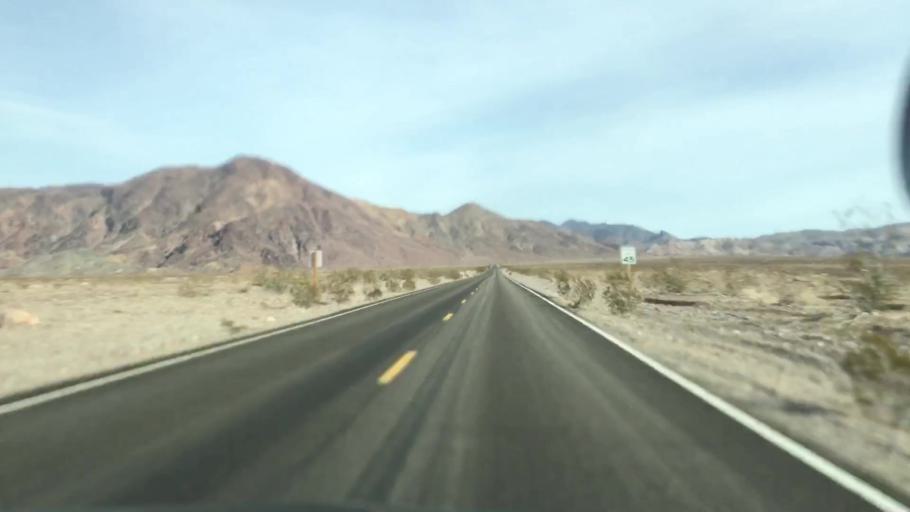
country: US
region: Nevada
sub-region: Nye County
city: Beatty
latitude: 36.6809
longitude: -117.0079
